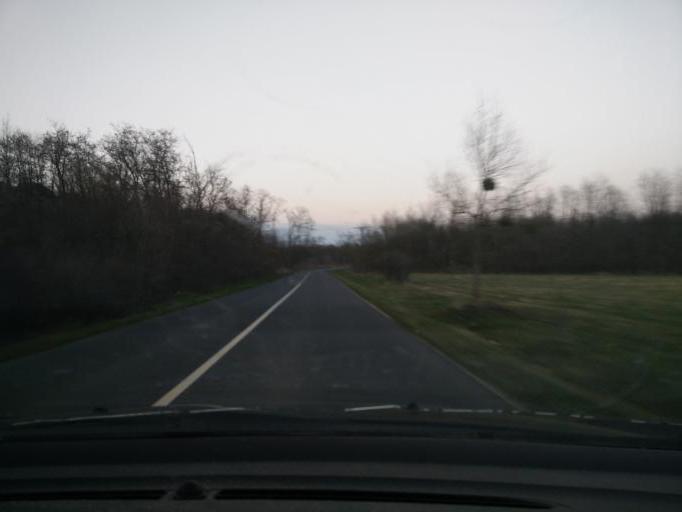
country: HU
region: Veszprem
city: Devecser
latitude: 47.0741
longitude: 17.3855
